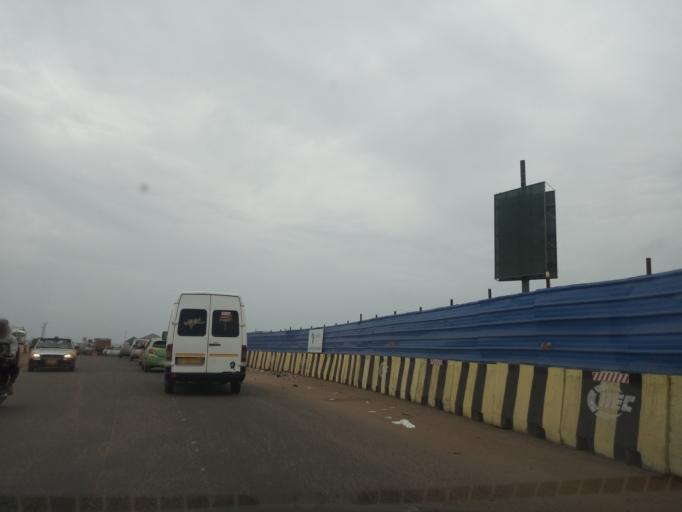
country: GH
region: Greater Accra
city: Tema
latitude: 5.6179
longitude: -0.0229
